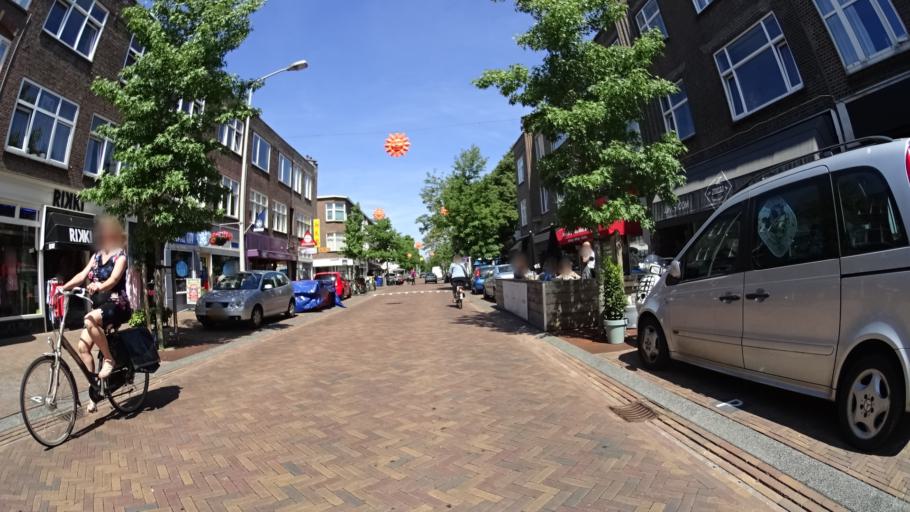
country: NL
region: South Holland
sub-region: Gemeente Den Haag
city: Scheveningen
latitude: 52.0795
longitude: 4.2686
